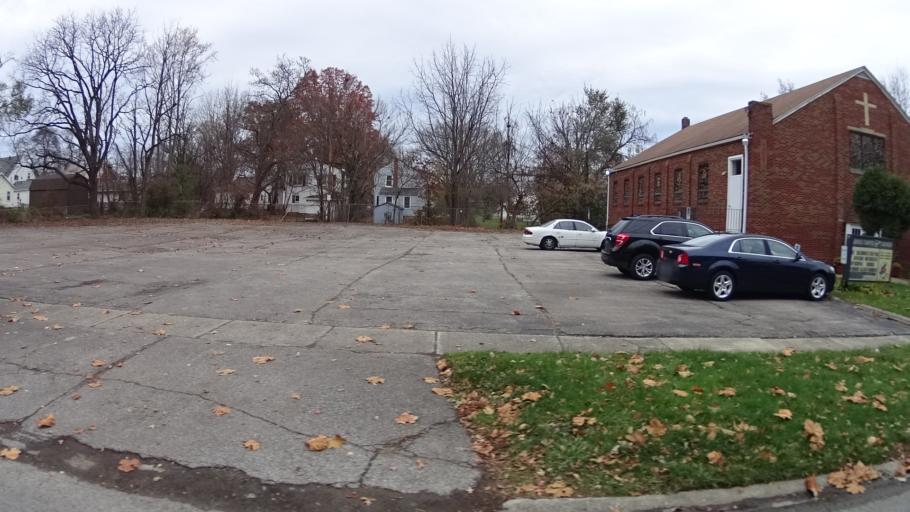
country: US
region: Ohio
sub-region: Lorain County
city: Elyria
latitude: 41.3511
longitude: -82.1098
